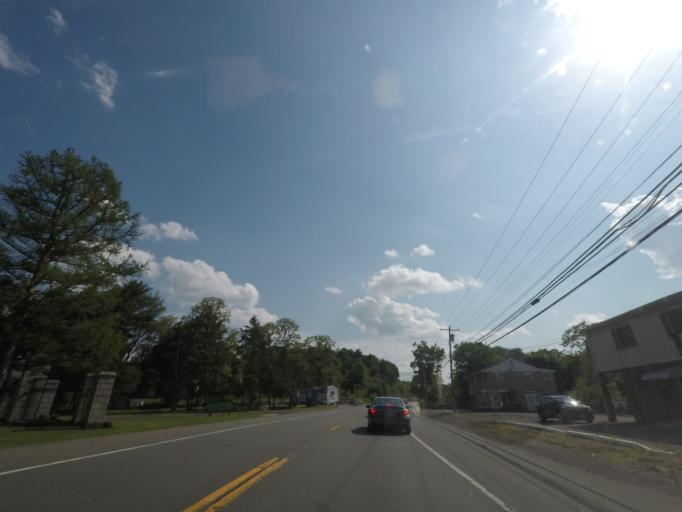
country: US
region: New York
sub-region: Ulster County
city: Marlboro
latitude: 41.5712
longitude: -73.9918
